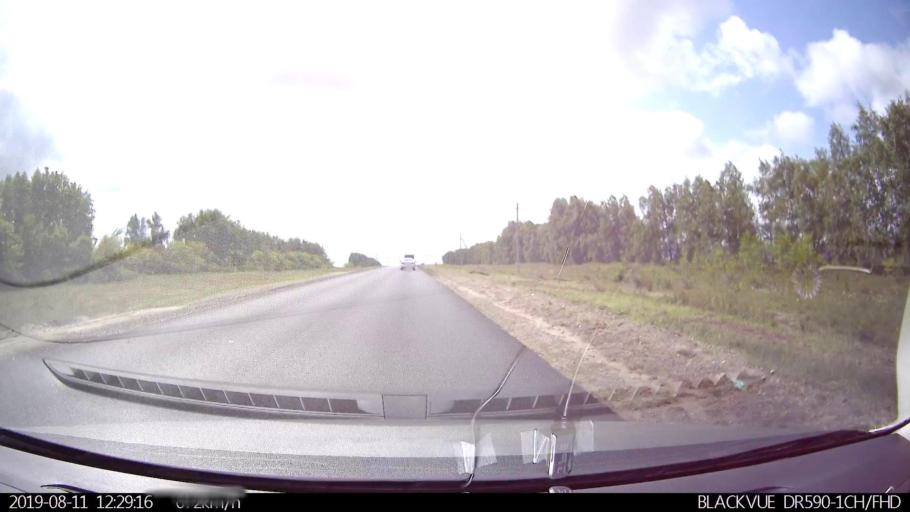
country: RU
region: Ulyanovsk
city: Ignatovka
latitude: 53.8365
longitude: 47.9040
